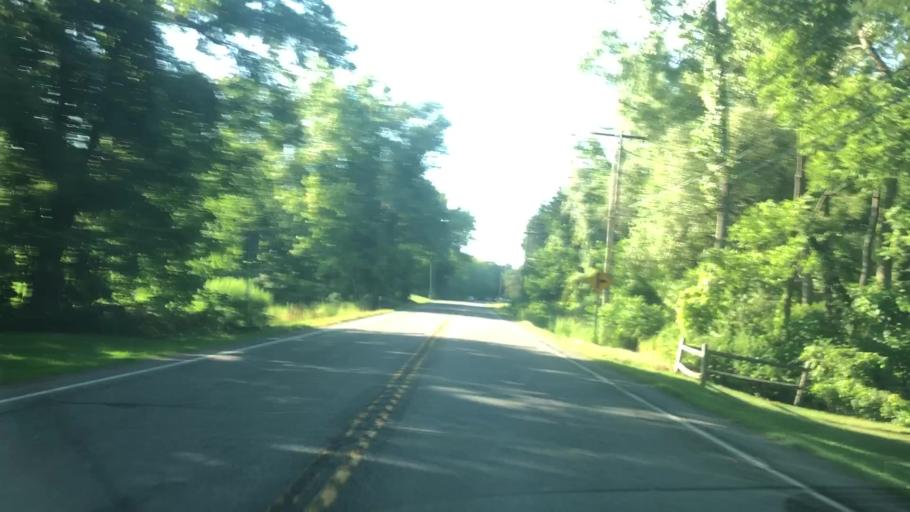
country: US
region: New York
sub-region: Wayne County
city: Ontario
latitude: 43.1846
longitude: -77.2894
